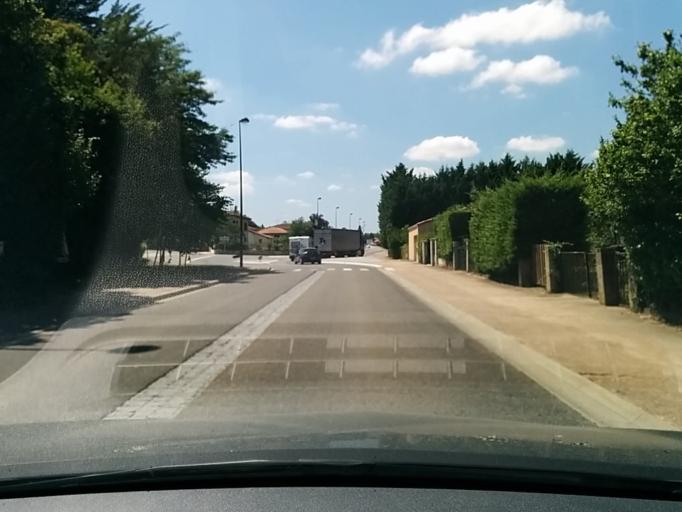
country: FR
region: Midi-Pyrenees
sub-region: Departement du Gers
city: Vic-Fezensac
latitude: 43.7556
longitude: 0.3014
